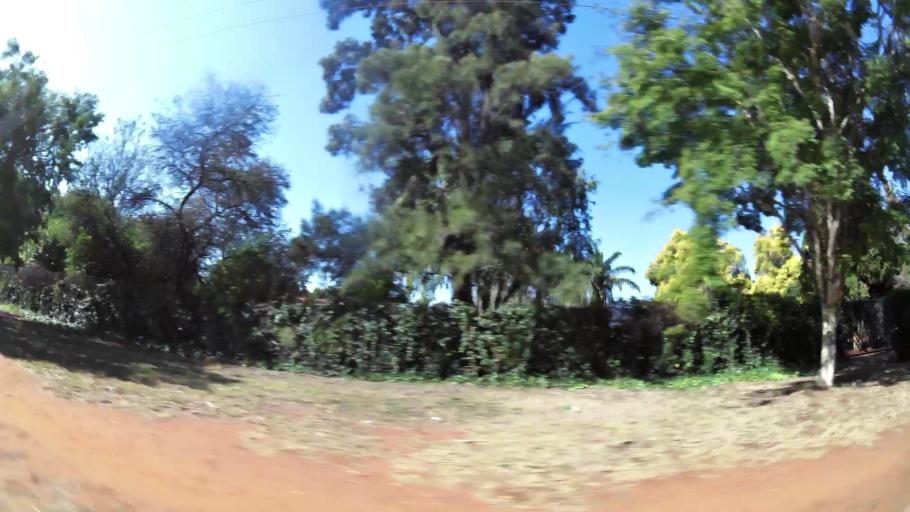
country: ZA
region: Gauteng
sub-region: City of Tshwane Metropolitan Municipality
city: Pretoria
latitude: -25.6543
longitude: 28.2626
